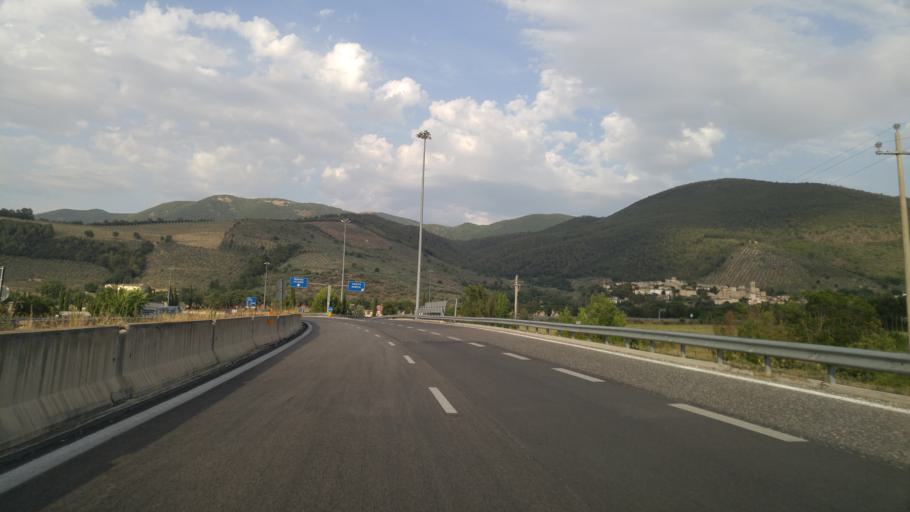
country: IT
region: Umbria
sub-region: Provincia di Perugia
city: San Giacomo
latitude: 42.7639
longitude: 12.7649
